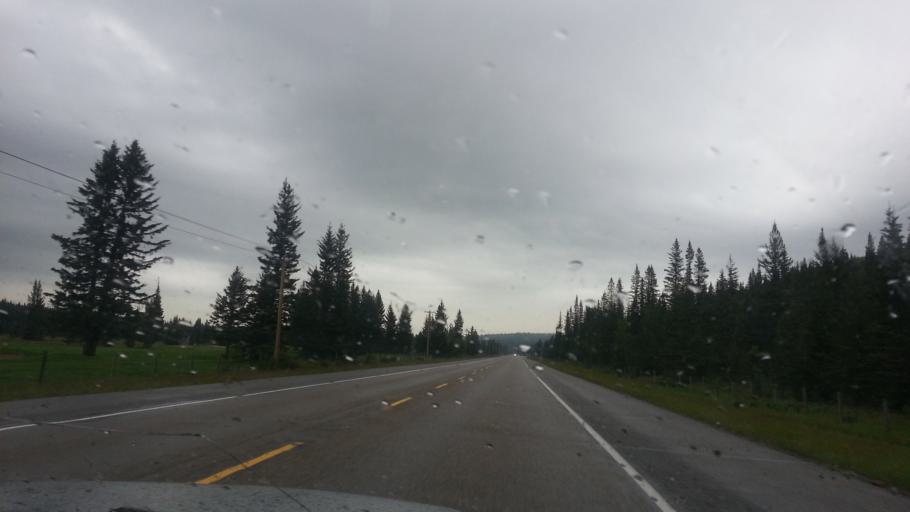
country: CA
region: Alberta
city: Cochrane
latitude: 50.9737
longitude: -114.5296
